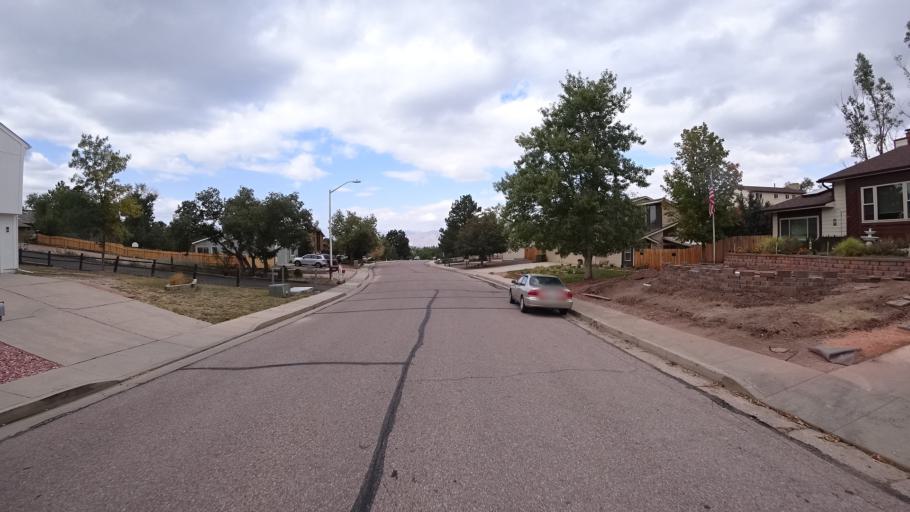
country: US
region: Colorado
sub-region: El Paso County
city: Cimarron Hills
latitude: 38.8916
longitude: -104.7290
